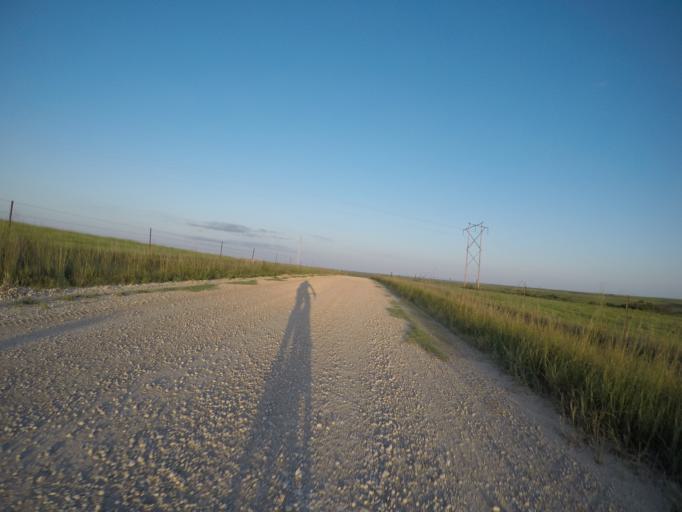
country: US
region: Kansas
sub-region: Riley County
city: Ogden
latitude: 39.0077
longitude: -96.6300
